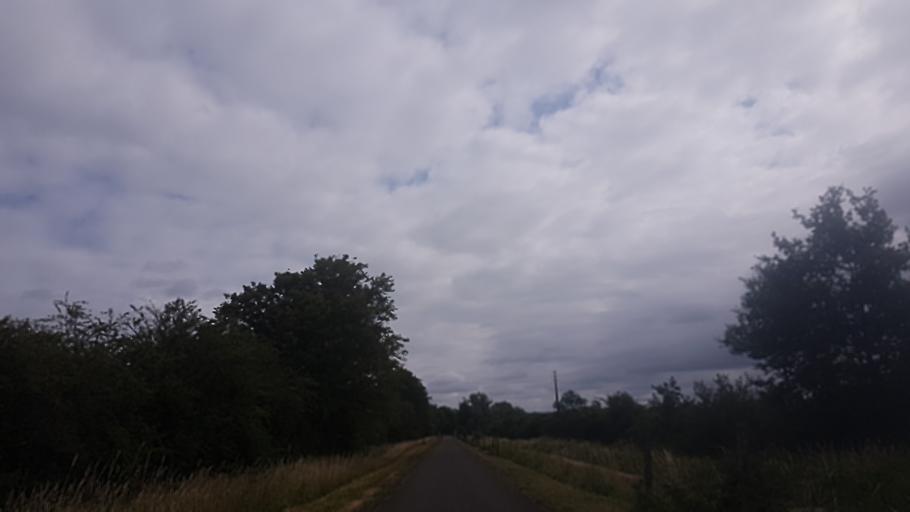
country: BE
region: Wallonia
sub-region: Province de Namur
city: Couvin
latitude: 50.1027
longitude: 4.5458
